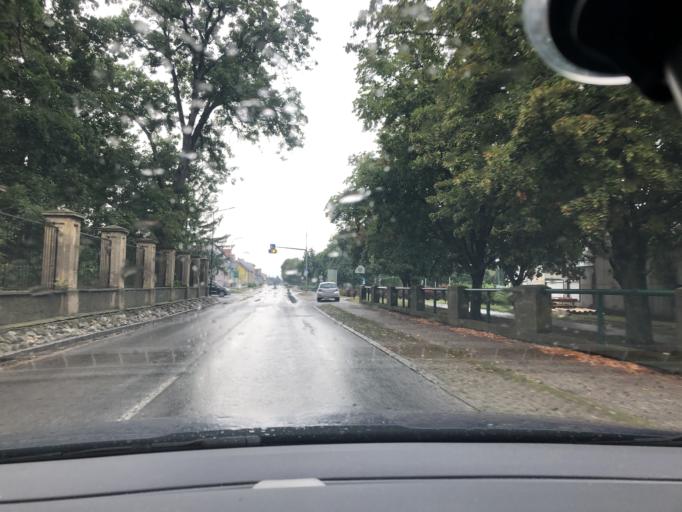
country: AT
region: Lower Austria
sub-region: Politischer Bezirk Ganserndorf
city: Ganserndorf
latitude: 48.3657
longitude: 16.6975
